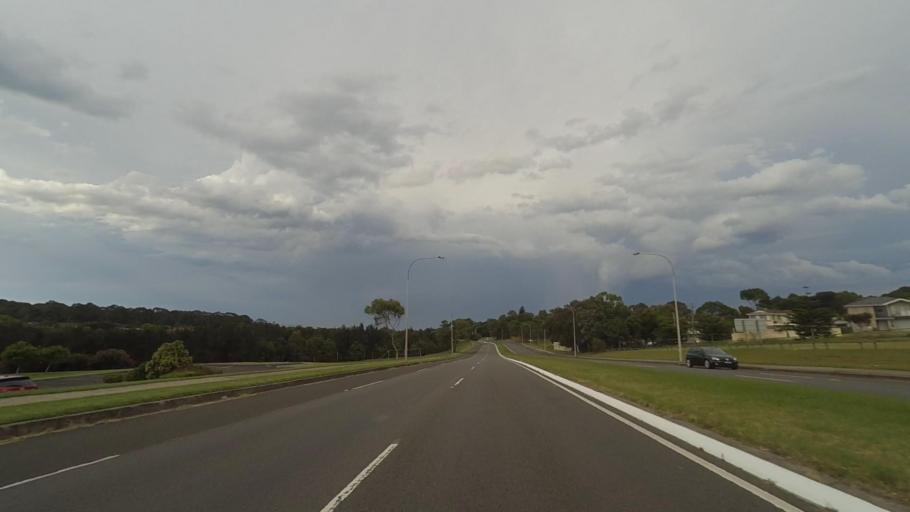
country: AU
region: New South Wales
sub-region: Shellharbour
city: Shellharbour Village
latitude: -34.5797
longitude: 150.8620
